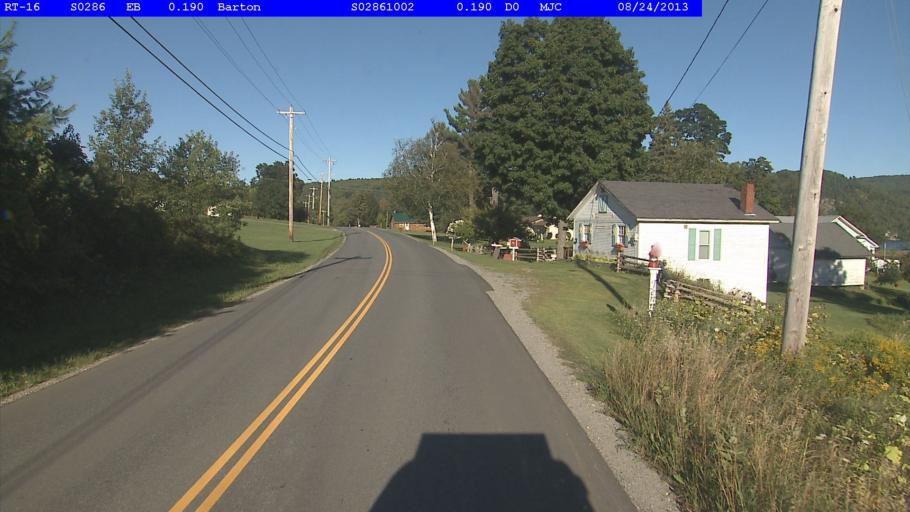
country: US
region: Vermont
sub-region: Orleans County
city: Newport
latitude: 44.7479
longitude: -72.1722
